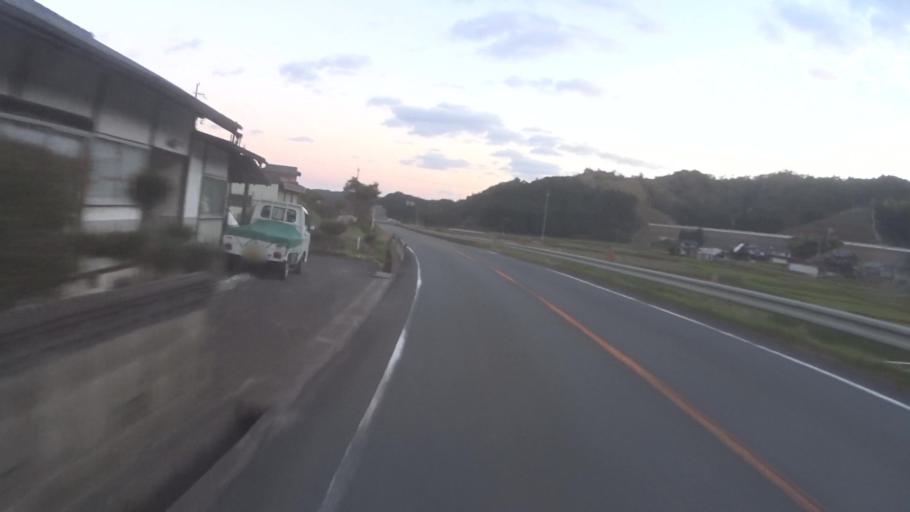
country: JP
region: Kyoto
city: Ayabe
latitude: 35.2067
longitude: 135.3519
